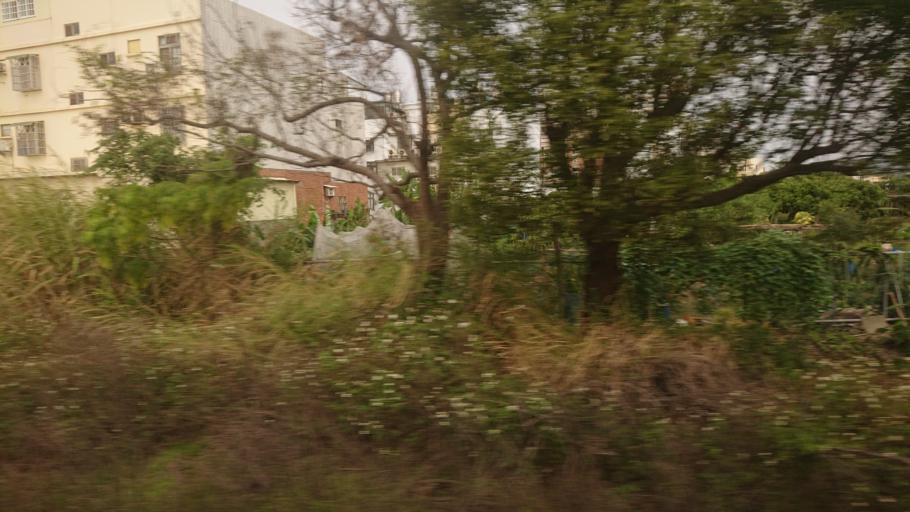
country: TW
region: Taiwan
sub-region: Changhua
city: Chang-hua
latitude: 24.0926
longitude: 120.5578
